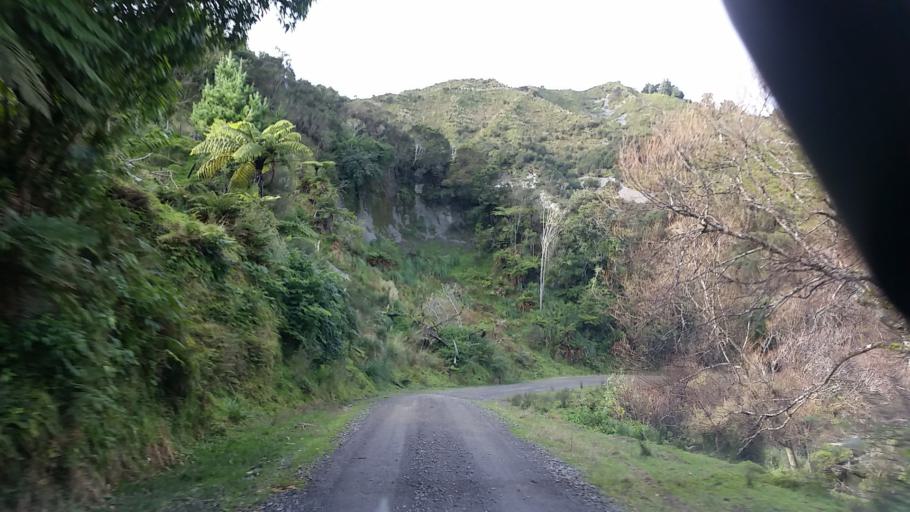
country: NZ
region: Taranaki
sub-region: New Plymouth District
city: Waitara
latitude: -39.0496
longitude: 174.5692
